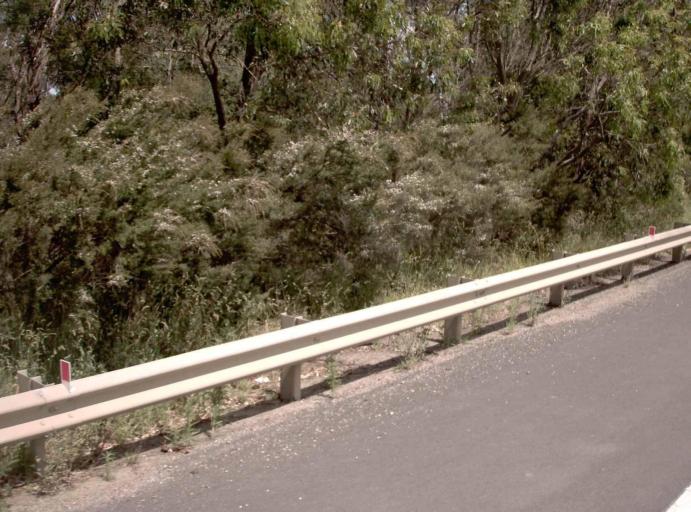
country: AU
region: Victoria
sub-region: Wellington
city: Heyfield
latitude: -38.1411
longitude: 146.7931
